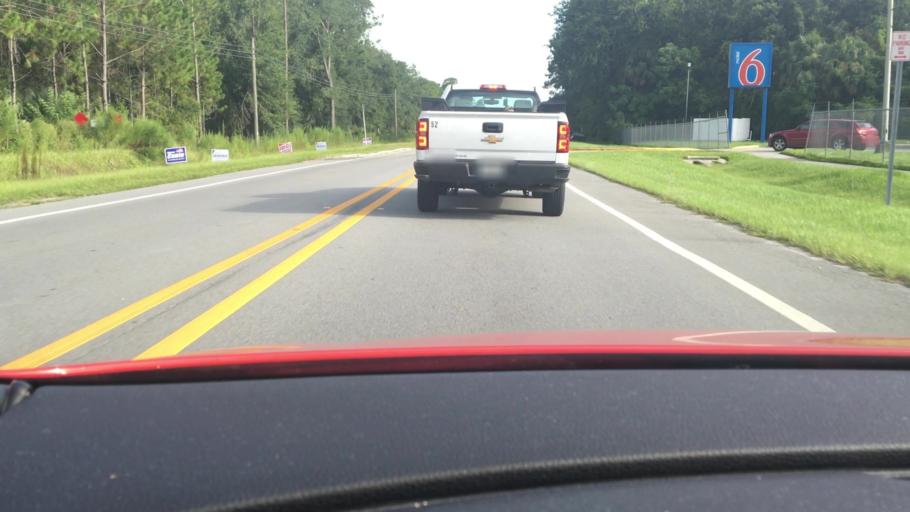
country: US
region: Florida
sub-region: Volusia County
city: Daytona Beach
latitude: 29.1694
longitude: -81.0880
